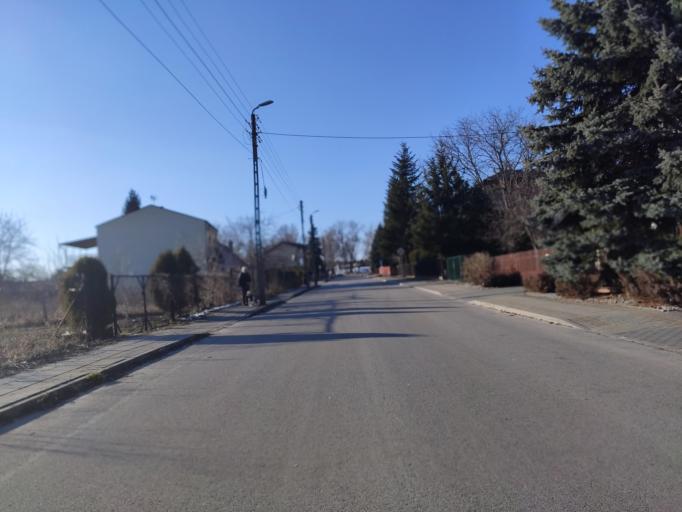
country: PL
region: Lublin Voivodeship
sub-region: Powiat lubartowski
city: Kock
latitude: 51.6424
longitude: 22.4418
